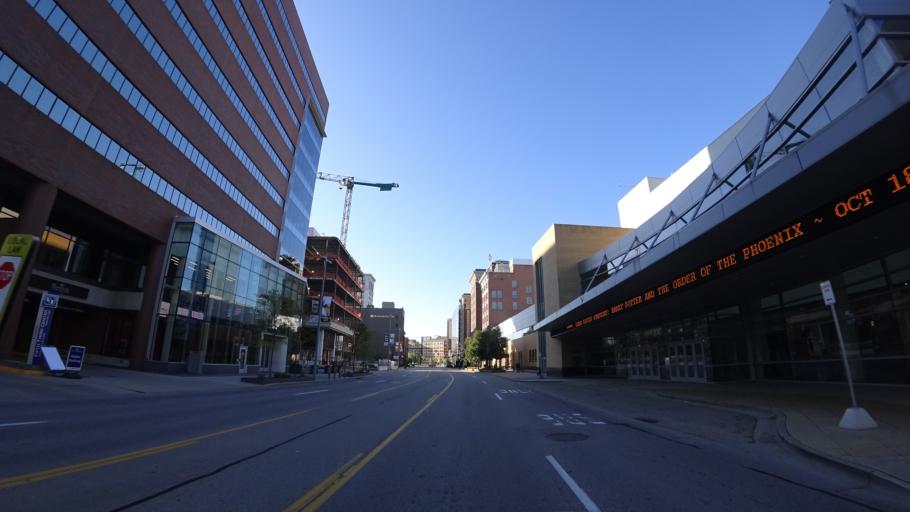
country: US
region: Michigan
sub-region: Kent County
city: Grand Rapids
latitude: 42.9684
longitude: -85.6722
